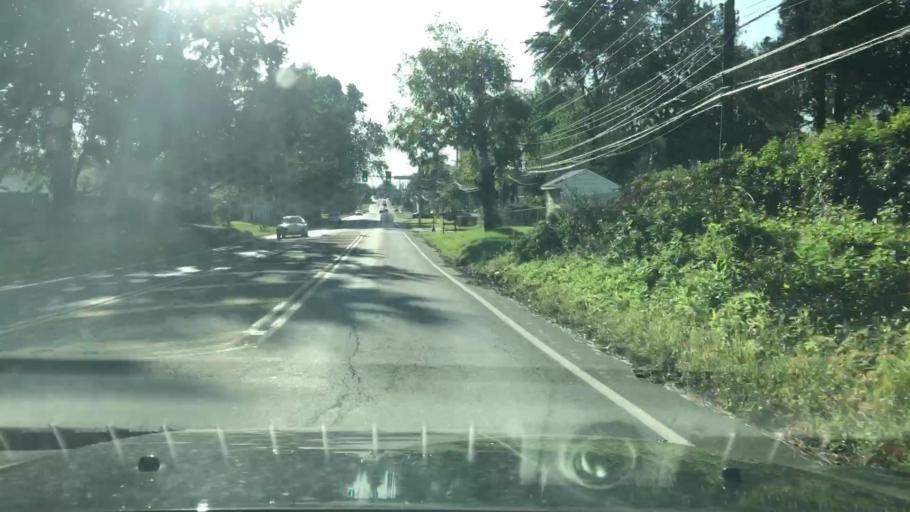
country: US
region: Pennsylvania
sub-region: Bucks County
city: Woodbourne
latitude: 40.1707
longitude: -74.8800
